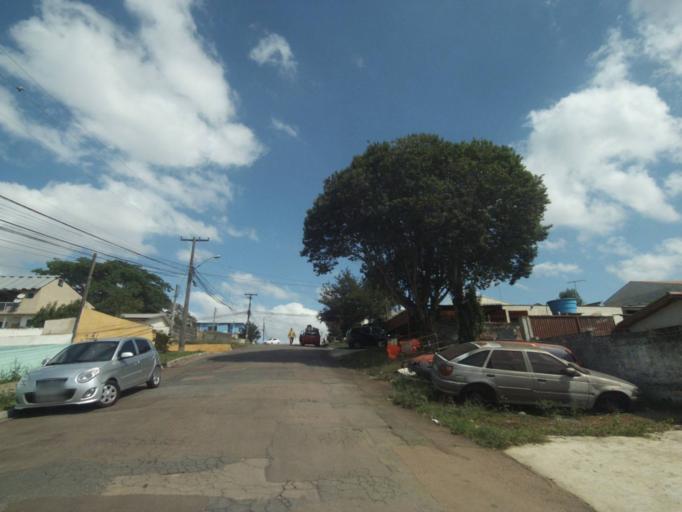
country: BR
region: Parana
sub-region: Curitiba
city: Curitiba
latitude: -25.4988
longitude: -49.3158
